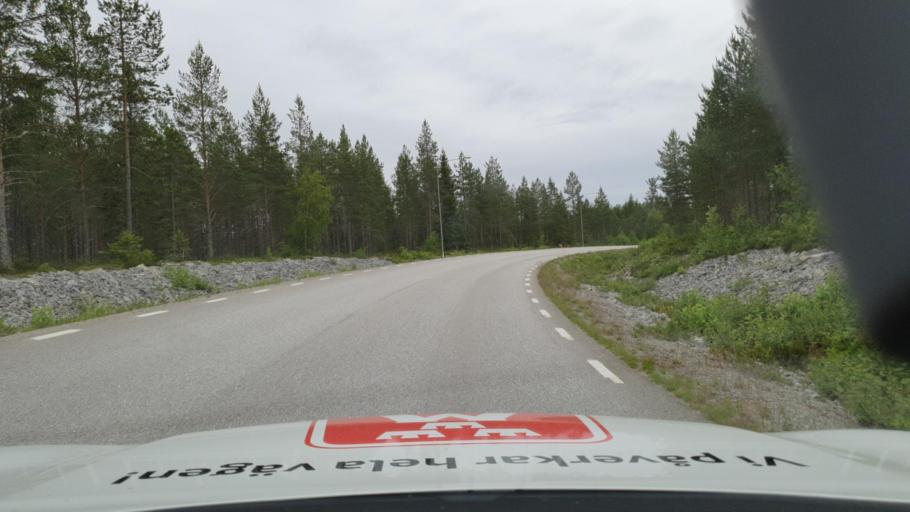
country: SE
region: Vaesterbotten
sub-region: Nordmalings Kommun
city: Nordmaling
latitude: 63.5357
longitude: 19.4052
